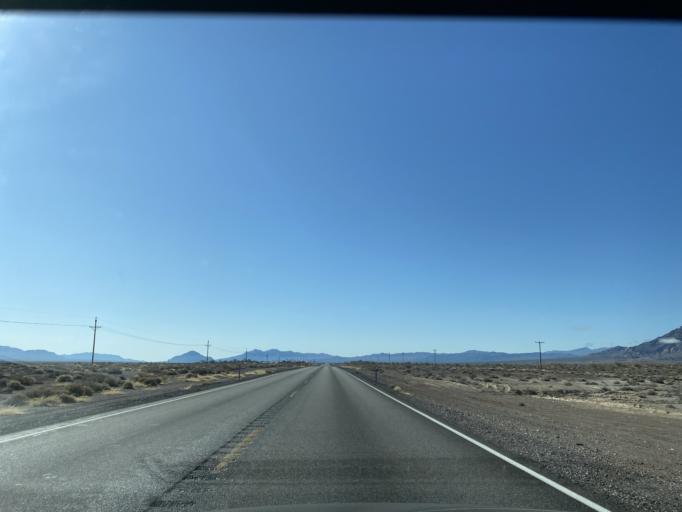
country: US
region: Nevada
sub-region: Nye County
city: Pahrump
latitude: 36.4305
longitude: -116.4221
